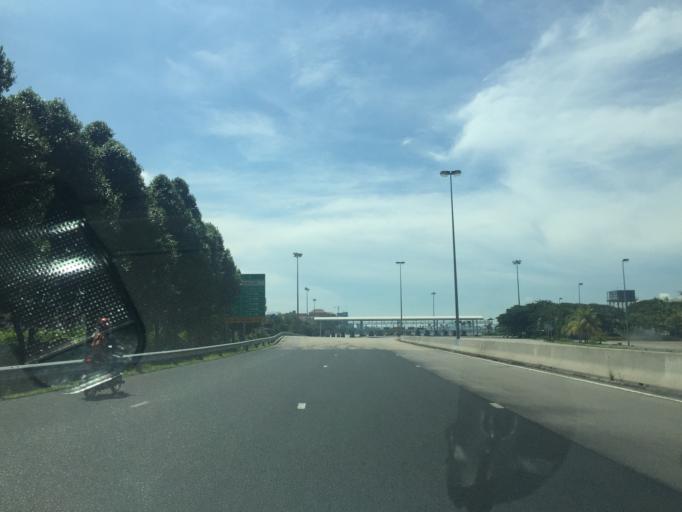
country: MY
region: Penang
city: Permatang Kuching
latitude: 5.4343
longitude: 100.3779
